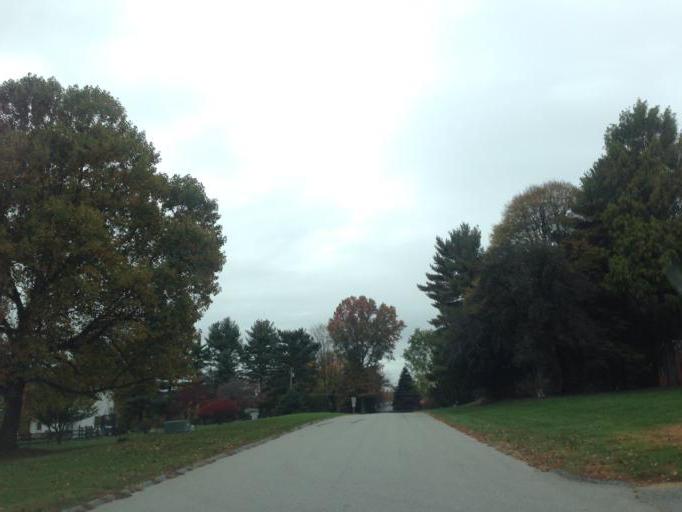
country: US
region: Maryland
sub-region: Howard County
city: Highland
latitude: 39.2732
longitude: -76.9569
